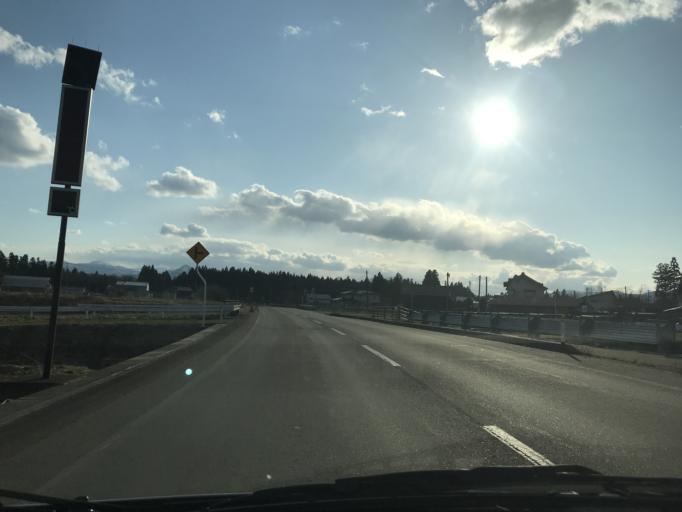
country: JP
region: Iwate
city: Hanamaki
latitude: 39.3352
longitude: 141.0423
